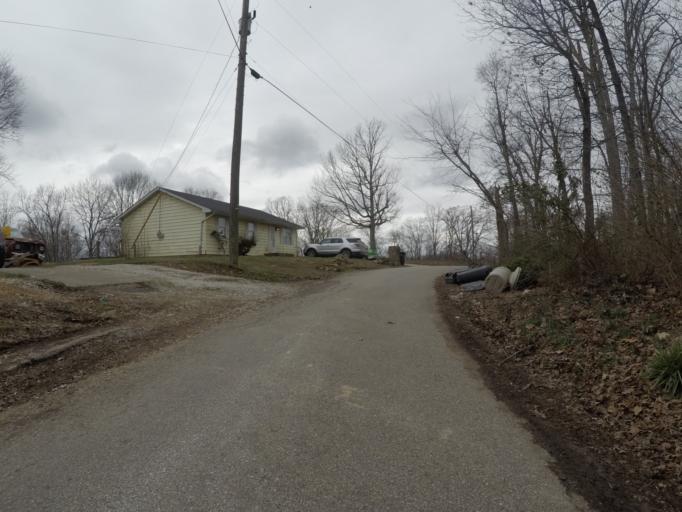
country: US
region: West Virginia
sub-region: Wayne County
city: Lavalette
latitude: 38.3673
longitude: -82.4226
